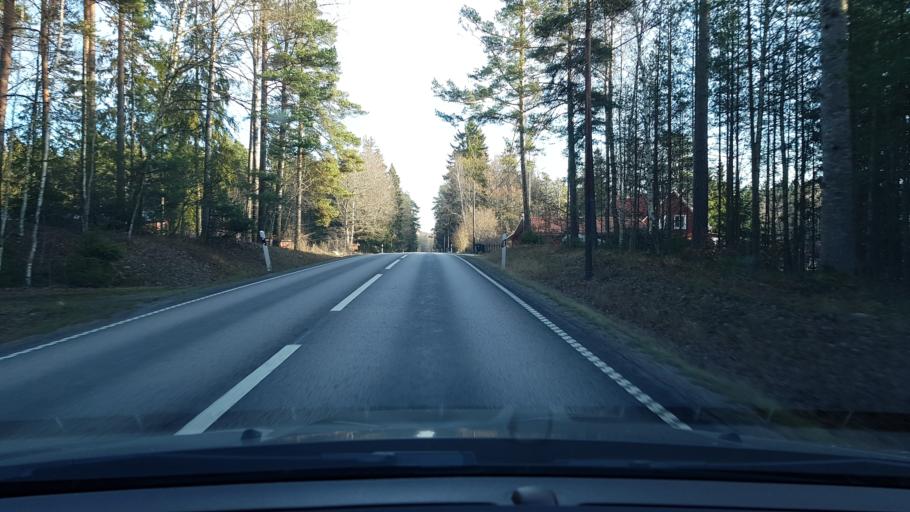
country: SE
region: Stockholm
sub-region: Norrtalje Kommun
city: Rimbo
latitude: 59.7402
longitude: 18.3225
